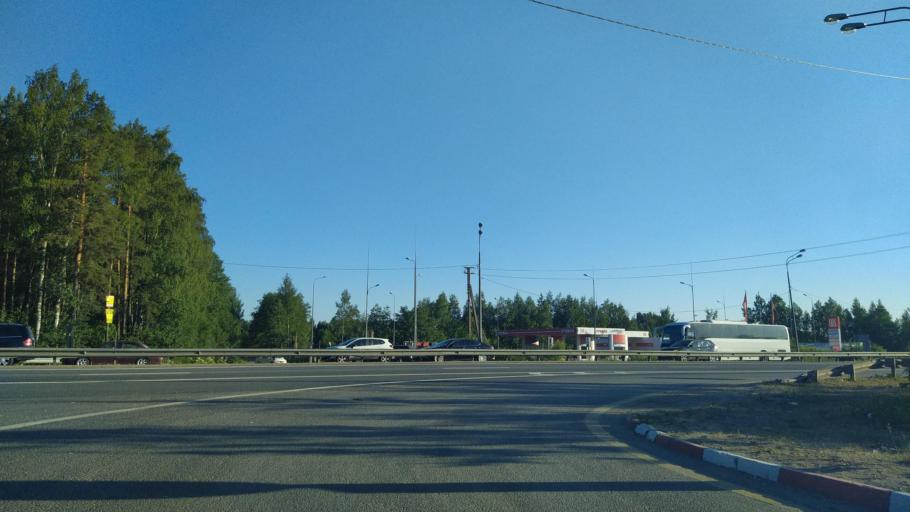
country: RU
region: Leningrad
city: Koltushi
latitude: 59.9008
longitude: 30.7330
